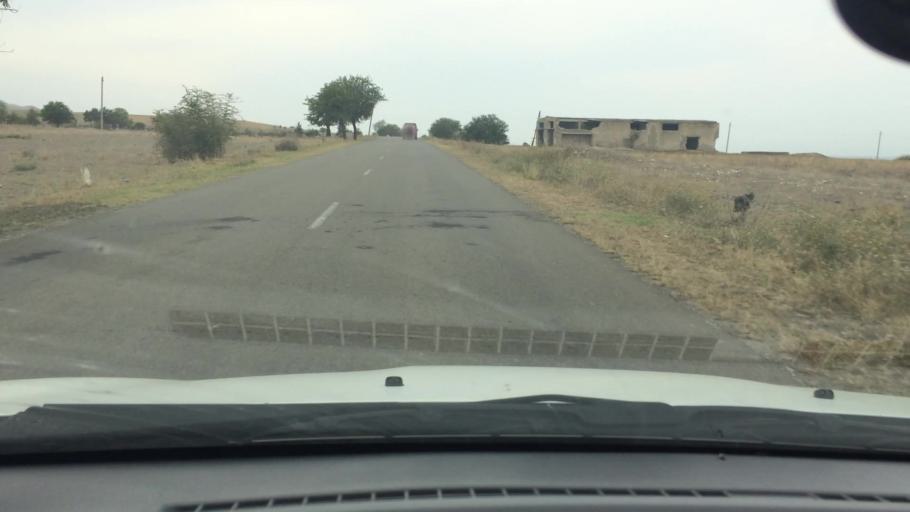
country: AM
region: Tavush
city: Berdavan
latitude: 41.3369
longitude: 45.0145
